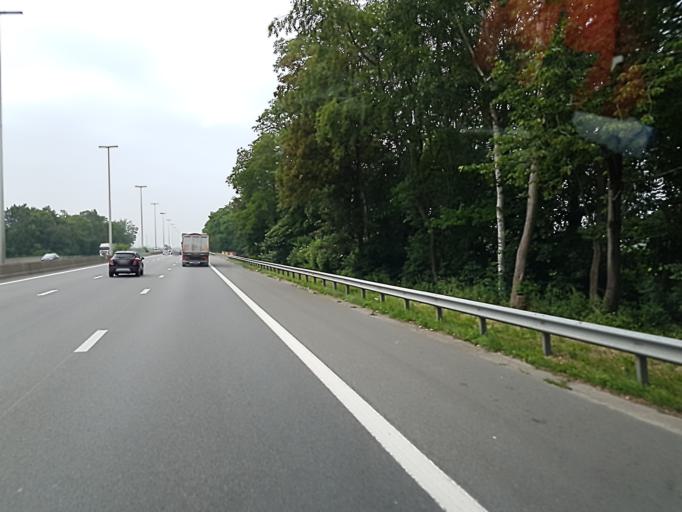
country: BE
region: Wallonia
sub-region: Province de Liege
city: Crisnee
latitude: 50.6917
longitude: 5.3985
